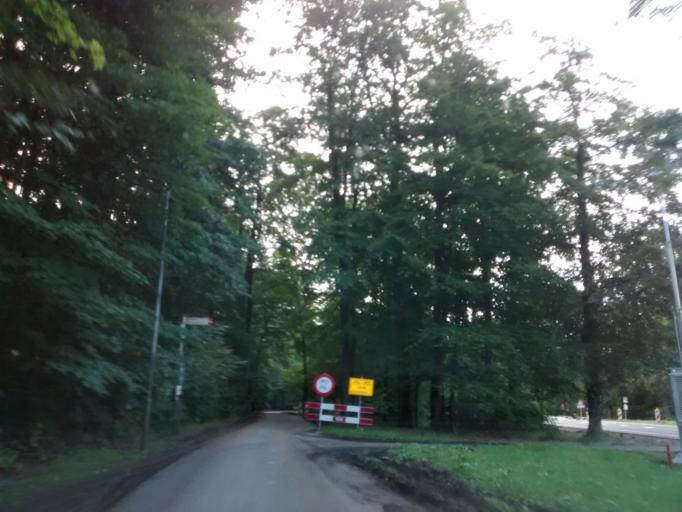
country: NL
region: Overijssel
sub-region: Gemeente Oldenzaal
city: Oldenzaal
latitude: 52.3200
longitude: 6.9711
